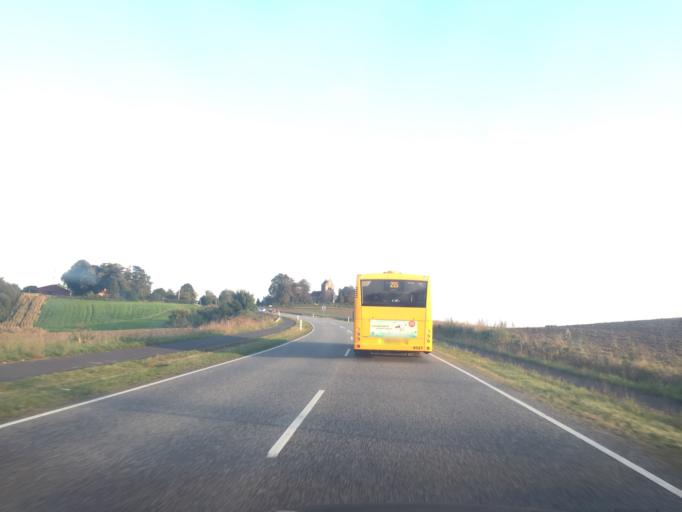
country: DK
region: Zealand
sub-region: Lejre Kommune
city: Osted
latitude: 55.5807
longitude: 11.9122
